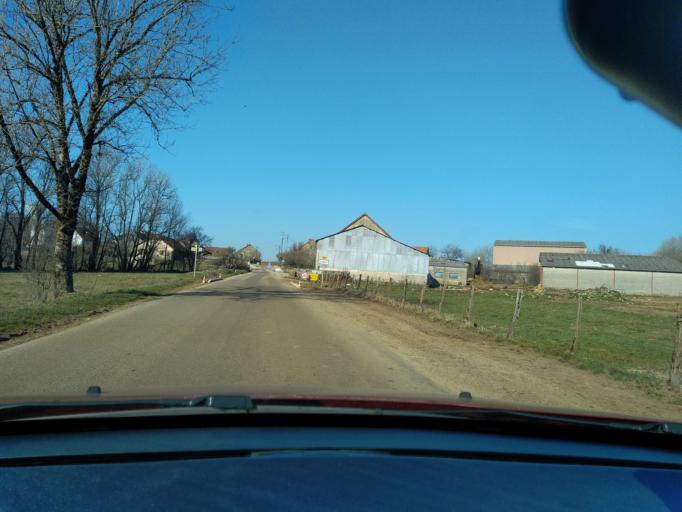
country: FR
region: Franche-Comte
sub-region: Departement du Jura
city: Perrigny
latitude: 46.6289
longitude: 5.6431
